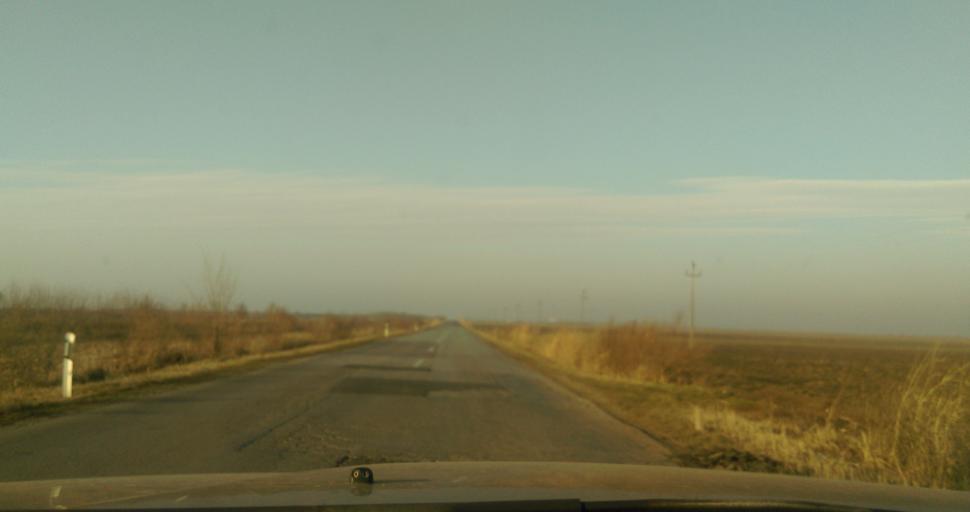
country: RS
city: Curug
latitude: 45.4879
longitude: 20.0374
